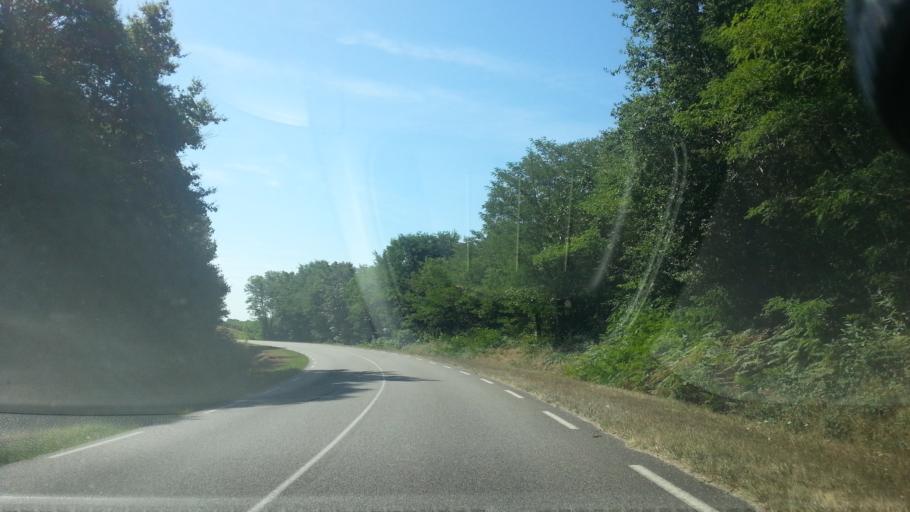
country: FR
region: Aquitaine
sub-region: Departement de la Gironde
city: Illats
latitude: 44.6066
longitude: -0.3743
